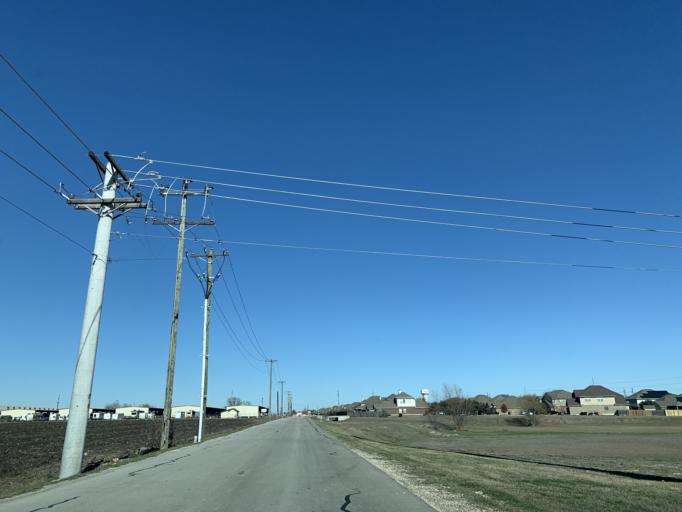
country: US
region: Texas
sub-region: Williamson County
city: Hutto
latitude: 30.5445
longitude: -97.5664
